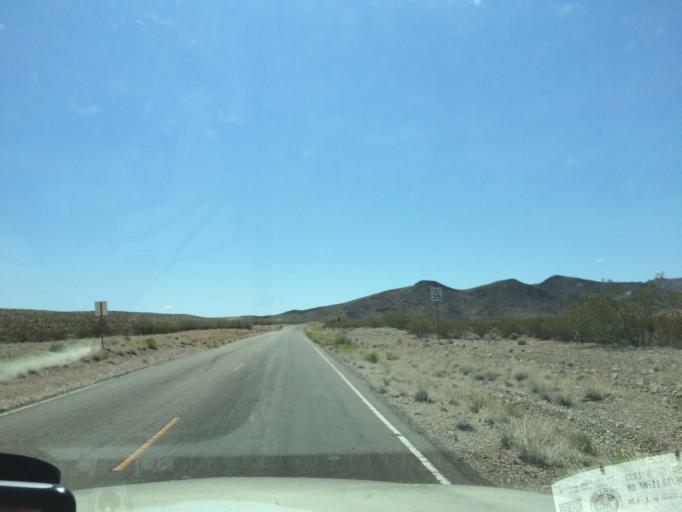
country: US
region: Nevada
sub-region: Clark County
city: Moapa Valley
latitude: 36.4474
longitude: -114.6751
